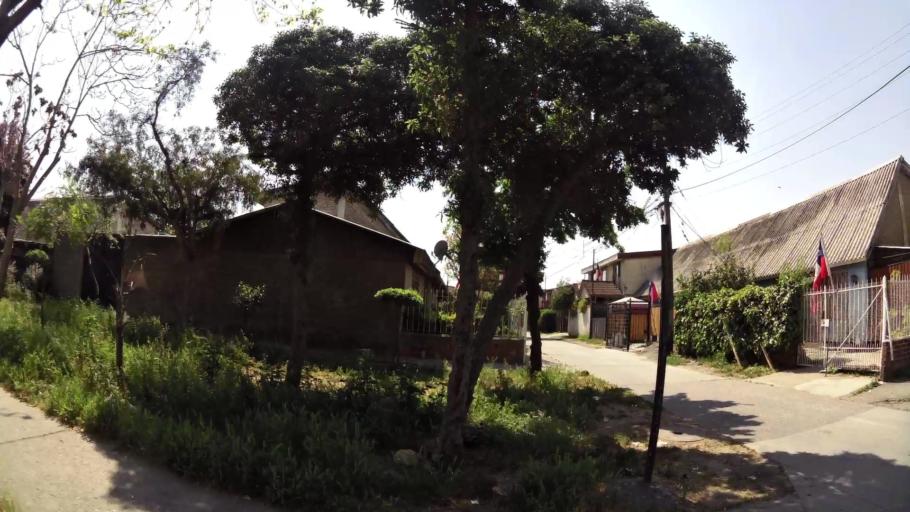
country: CL
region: Santiago Metropolitan
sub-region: Provincia de Santiago
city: La Pintana
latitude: -33.5520
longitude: -70.6121
